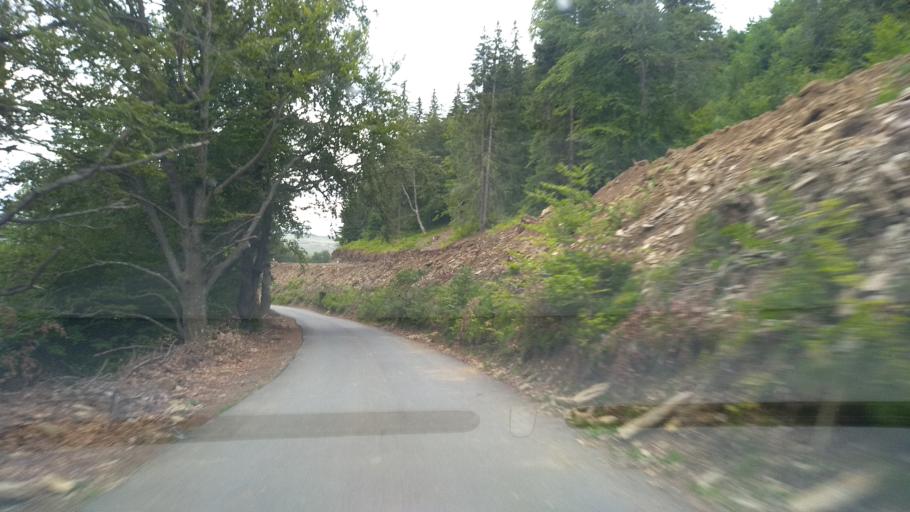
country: RO
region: Hunedoara
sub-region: Municipiul  Vulcan
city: Jiu-Paroseni
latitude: 45.3237
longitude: 23.2923
